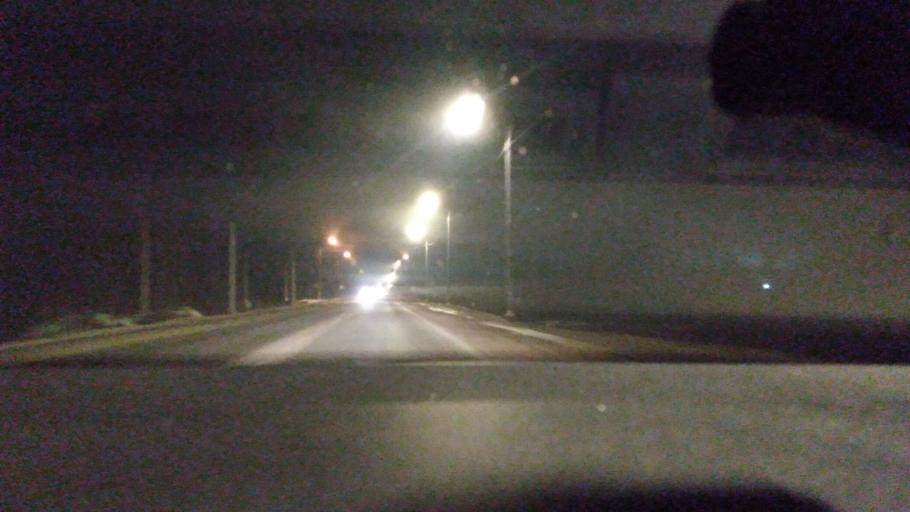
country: RU
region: Moskovskaya
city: Yegor'yevsk
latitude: 55.4076
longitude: 39.0534
